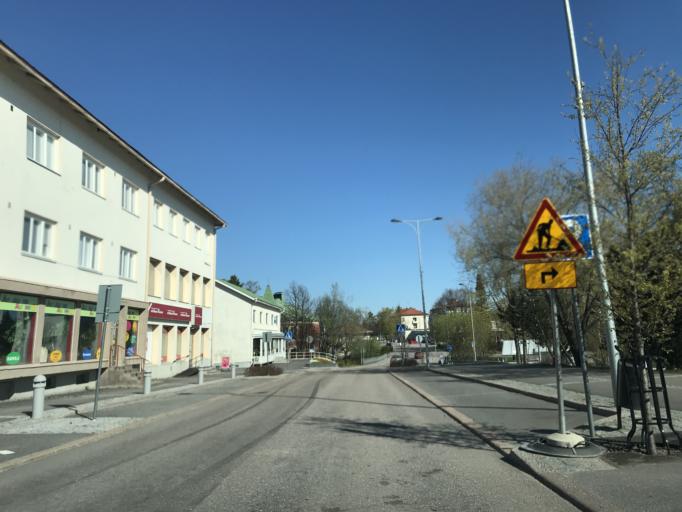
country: FI
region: Paijanne Tavastia
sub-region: Lahti
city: Orimattila
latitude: 60.8025
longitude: 25.7346
